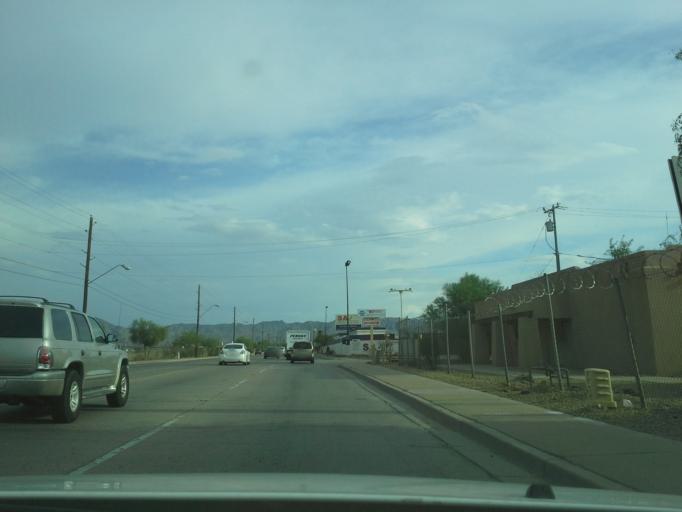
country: US
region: Arizona
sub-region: Maricopa County
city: Phoenix
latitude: 33.4189
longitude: -112.0998
